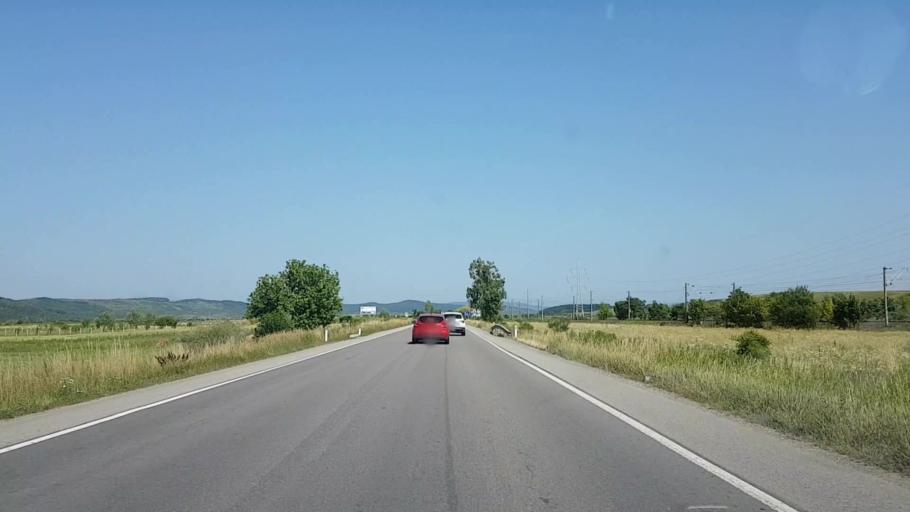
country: RO
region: Bistrita-Nasaud
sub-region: Comuna Sintereag
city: Cociu
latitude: 47.1839
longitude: 24.2135
